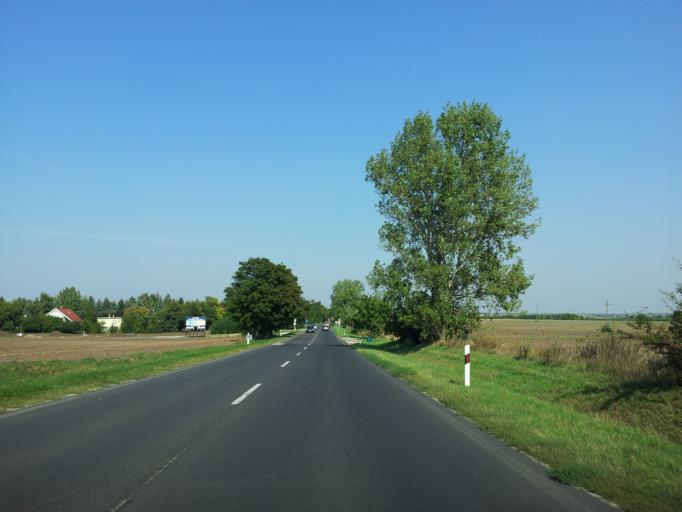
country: HU
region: Somogy
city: Balatonszabadi
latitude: 46.9263
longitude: 18.1146
